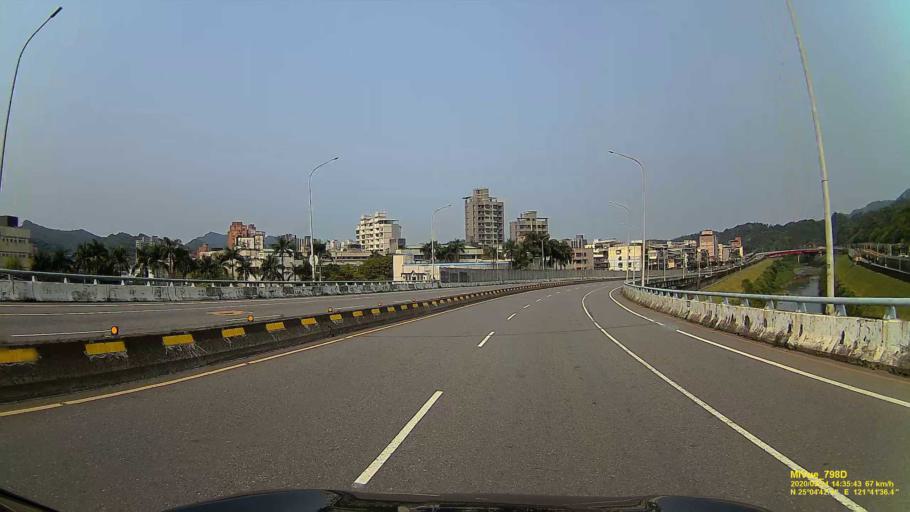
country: TW
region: Taiwan
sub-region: Keelung
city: Keelung
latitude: 25.0786
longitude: 121.6936
